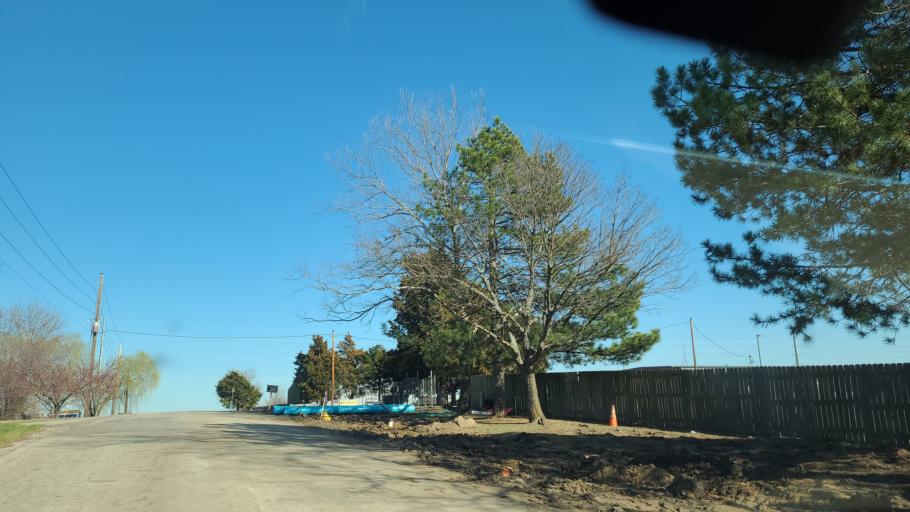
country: US
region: Kansas
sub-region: Douglas County
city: Lawrence
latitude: 38.9500
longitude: -95.2067
